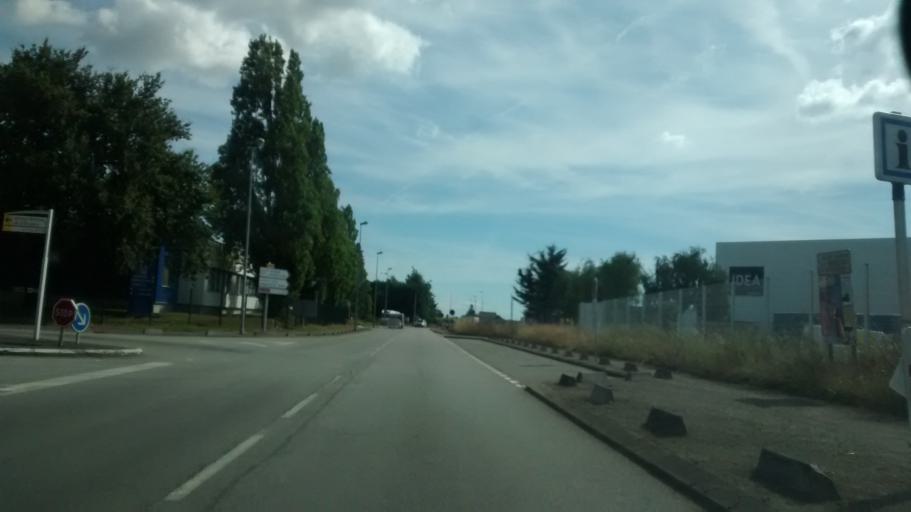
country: FR
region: Pays de la Loire
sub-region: Departement de la Loire-Atlantique
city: Bouguenais
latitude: 47.1552
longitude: -1.5983
